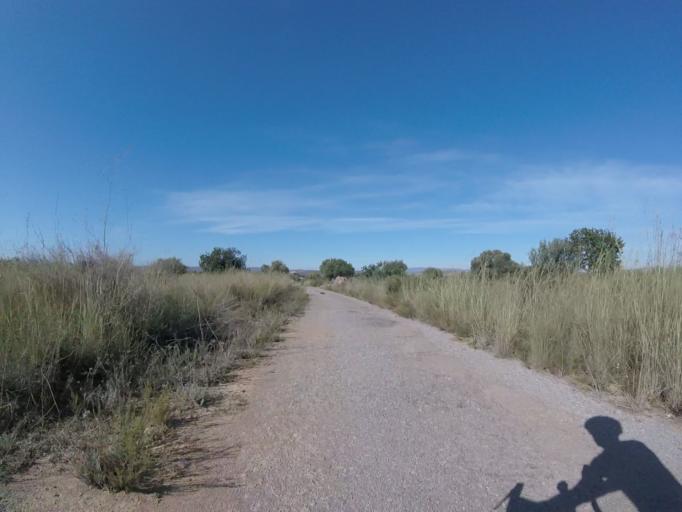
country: ES
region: Valencia
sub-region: Provincia de Castello
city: Torreblanca
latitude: 40.2078
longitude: 0.2449
